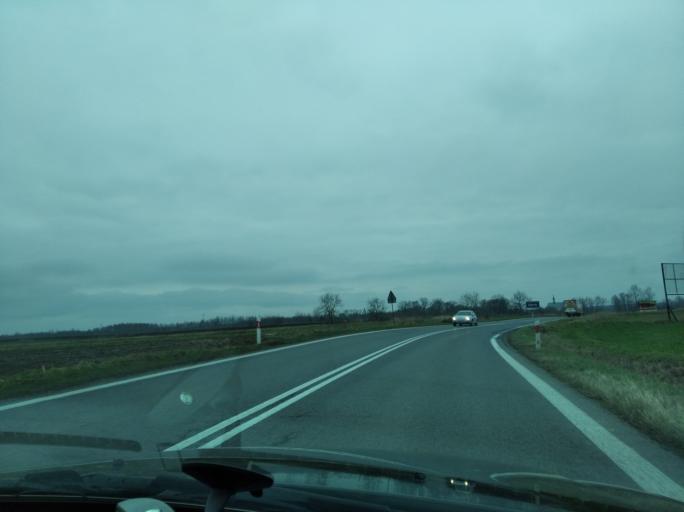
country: PL
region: Subcarpathian Voivodeship
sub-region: Powiat lancucki
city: Zolynia
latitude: 50.1746
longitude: 22.3140
